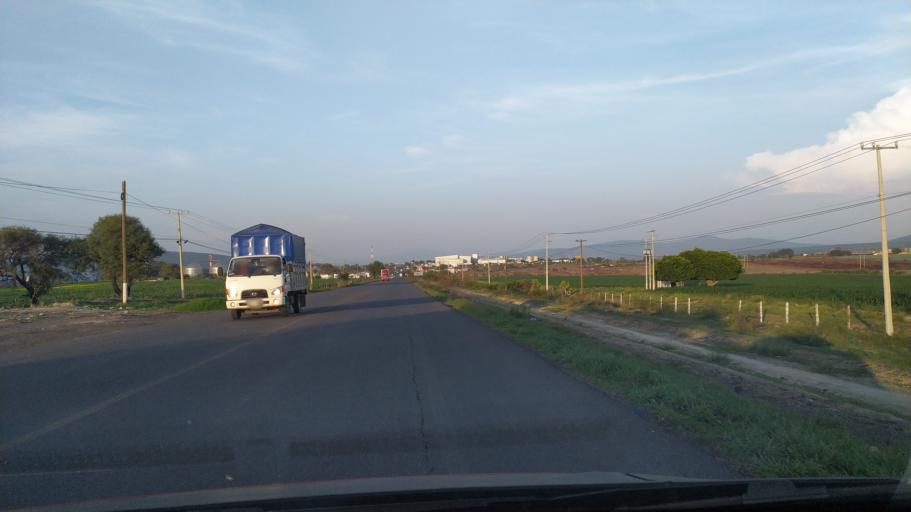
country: MX
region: Michoacan
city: Vistahermosa de Negrete
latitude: 20.2665
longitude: -102.4616
